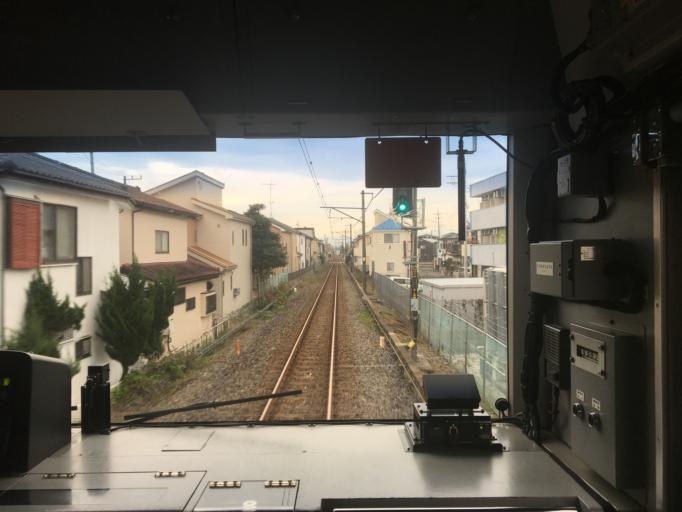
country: JP
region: Saitama
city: Kawagoe
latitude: 35.9202
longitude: 139.4423
